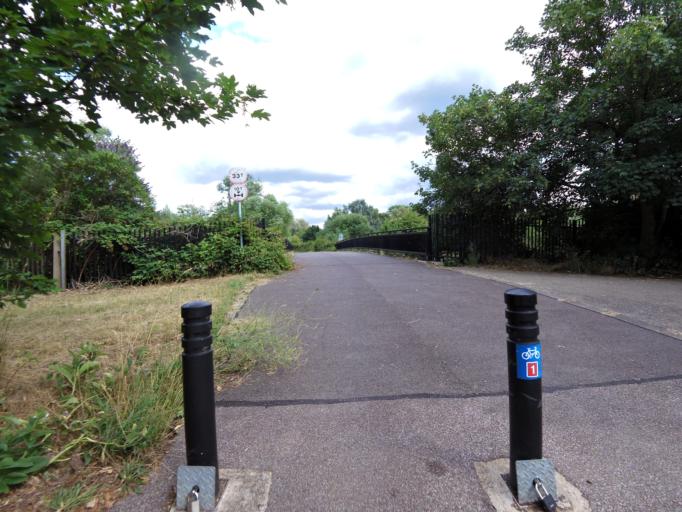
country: GB
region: England
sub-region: Essex
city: Waltham Abbey
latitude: 51.6666
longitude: -0.0117
